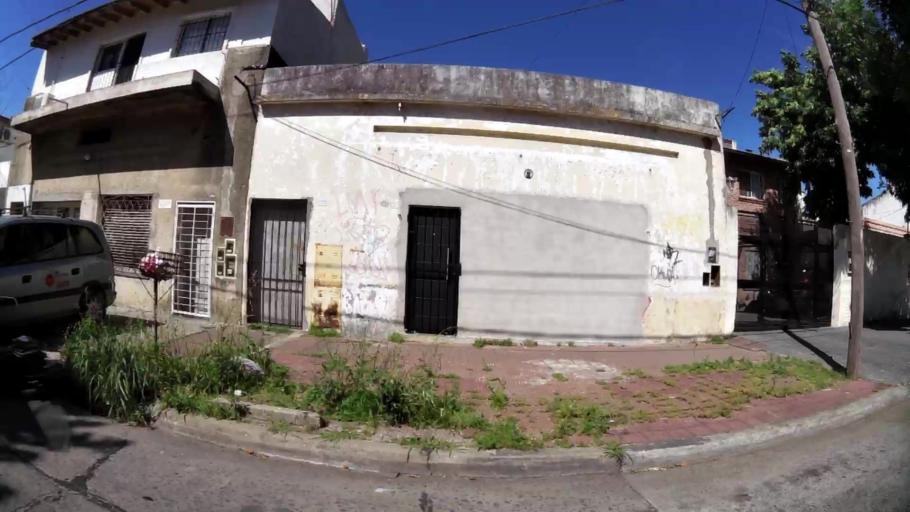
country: AR
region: Buenos Aires
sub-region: Partido de General San Martin
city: General San Martin
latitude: -34.5395
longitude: -58.5748
